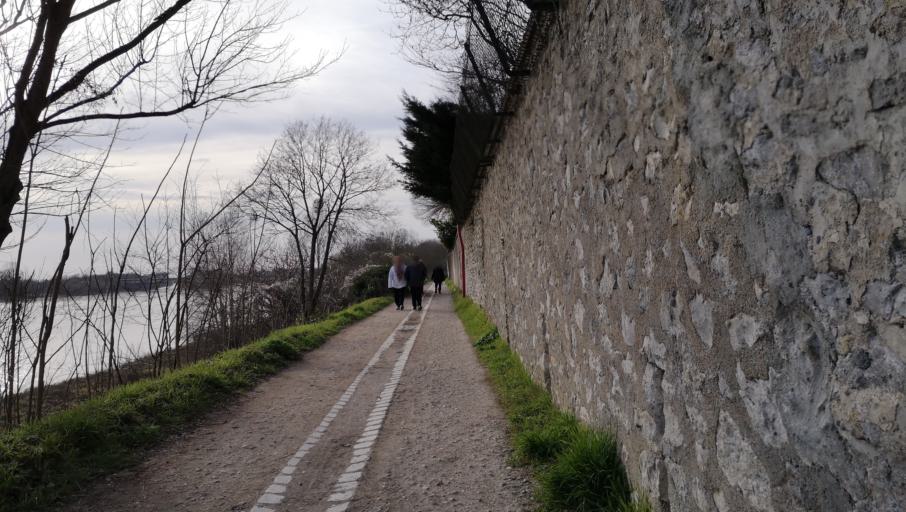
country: FR
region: Centre
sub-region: Departement du Loiret
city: Saint-Pryve-Saint-Mesmin
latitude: 47.8964
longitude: 1.8693
